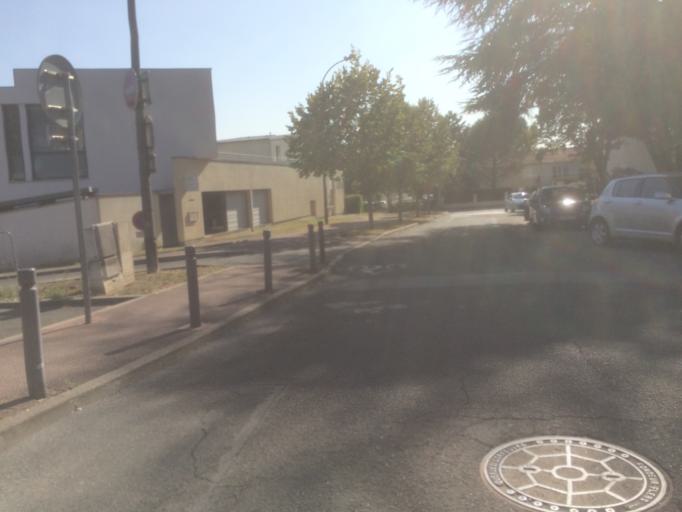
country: FR
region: Ile-de-France
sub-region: Departement de l'Essonne
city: Longjumeau
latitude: 48.6935
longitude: 2.3154
